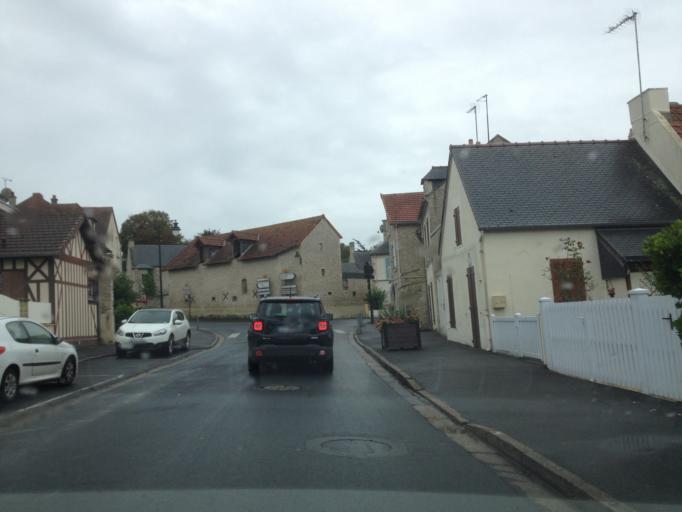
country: FR
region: Lower Normandy
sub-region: Departement du Calvados
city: Saint-Vigor-le-Grand
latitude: 49.3384
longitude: -0.6210
